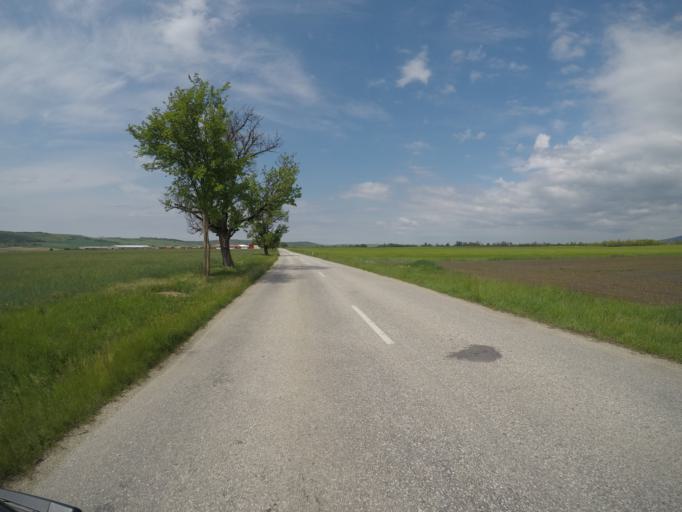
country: HU
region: Komarom-Esztergom
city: Esztergom
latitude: 47.9140
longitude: 18.7529
